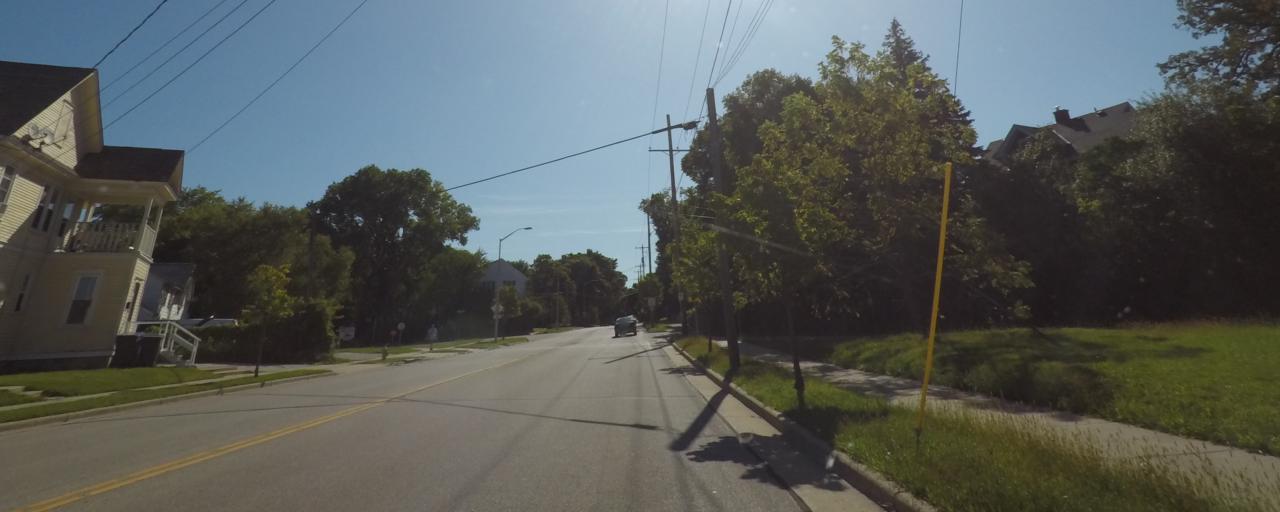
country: US
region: Wisconsin
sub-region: Waukesha County
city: Waukesha
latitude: 43.0075
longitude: -88.2210
